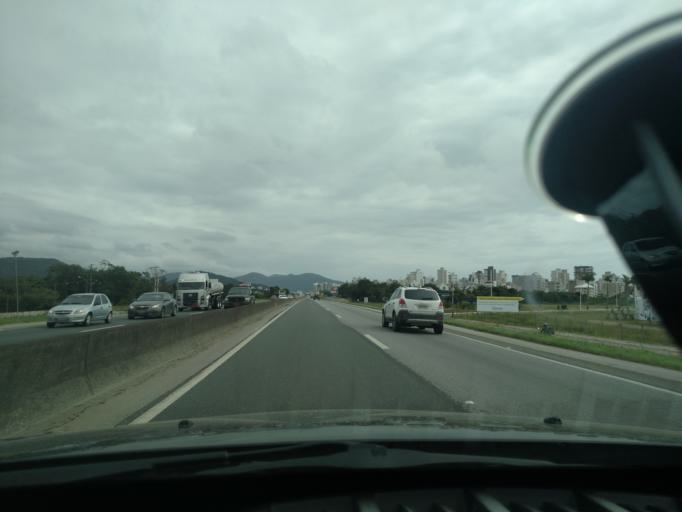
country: BR
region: Santa Catarina
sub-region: Itapema
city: Itapema
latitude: -27.1412
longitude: -48.6102
